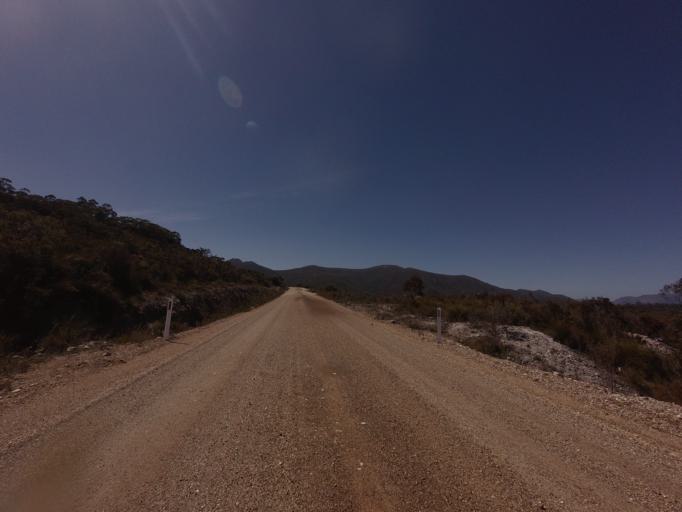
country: AU
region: Tasmania
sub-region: Huon Valley
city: Geeveston
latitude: -43.0371
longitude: 146.3283
